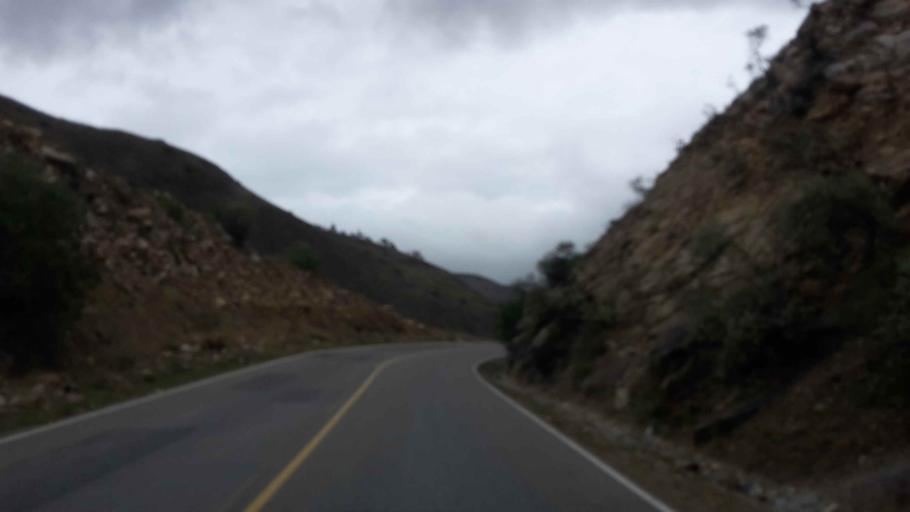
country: BO
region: Cochabamba
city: Punata
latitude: -17.4986
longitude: -65.7944
